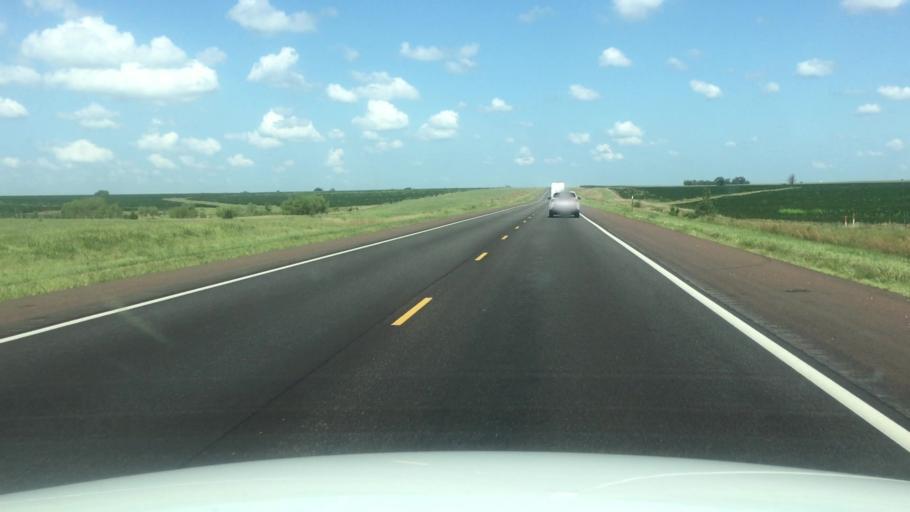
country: US
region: Kansas
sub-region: Nemaha County
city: Sabetha
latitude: 39.8575
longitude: -95.7578
